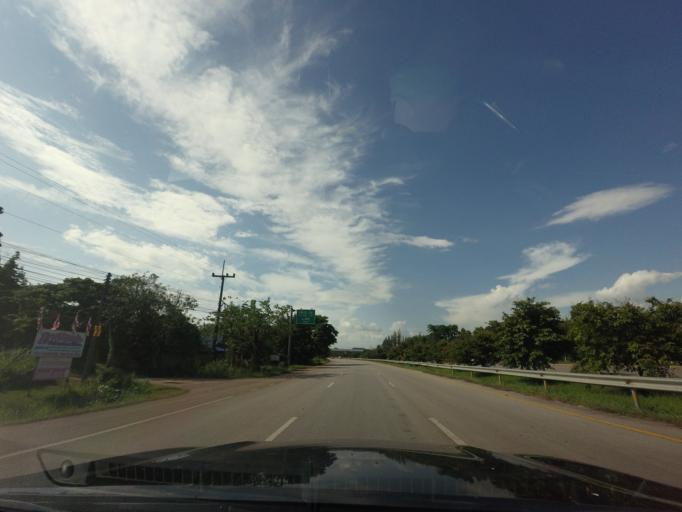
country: TH
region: Nong Khai
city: Sa Khrai
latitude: 17.6738
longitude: 102.7898
